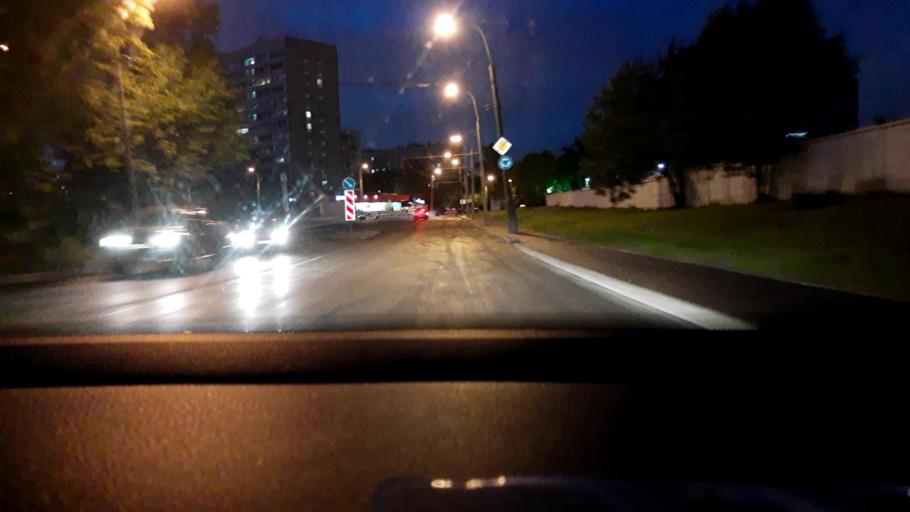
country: RU
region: Moskovskaya
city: Novogireyevo
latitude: 55.7487
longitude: 37.8301
